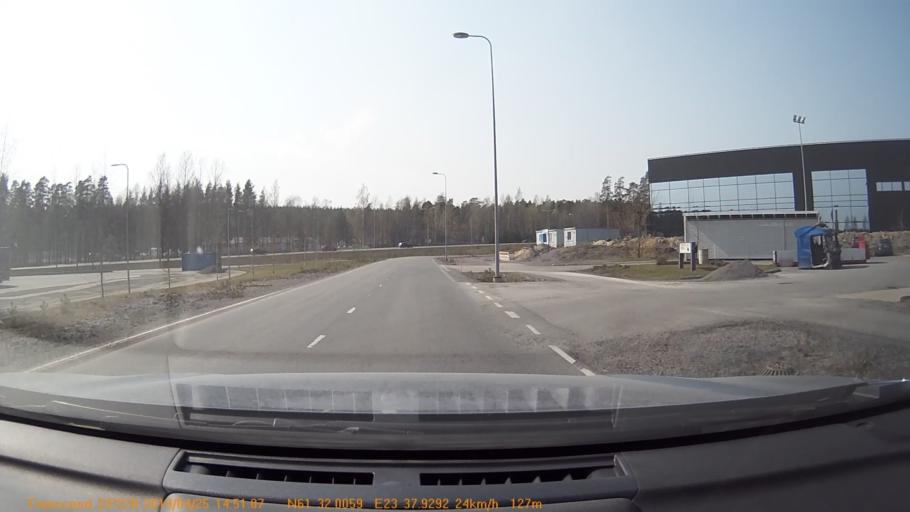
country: FI
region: Pirkanmaa
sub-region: Tampere
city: Yloejaervi
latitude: 61.5333
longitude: 23.6318
